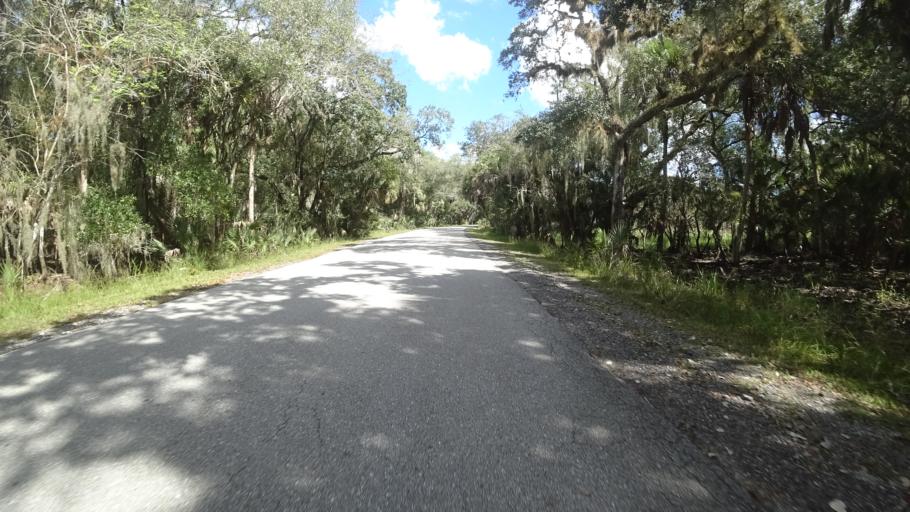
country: US
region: Florida
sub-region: Sarasota County
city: Lake Sarasota
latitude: 27.2469
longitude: -82.3009
